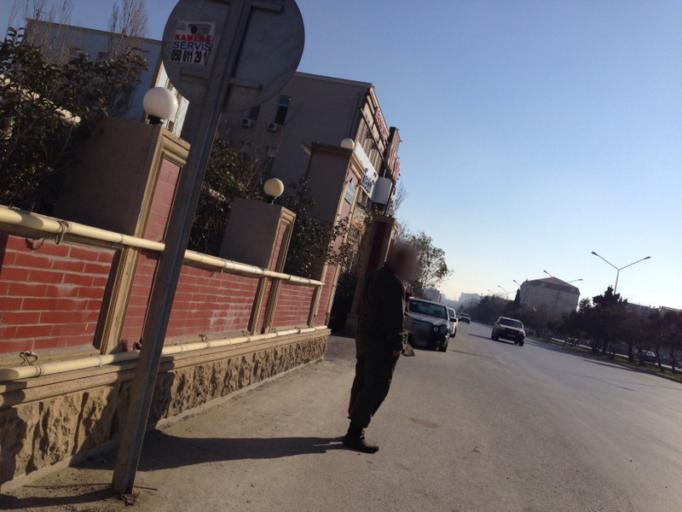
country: AZ
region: Baki
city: Binagadi
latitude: 40.4197
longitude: 49.8559
